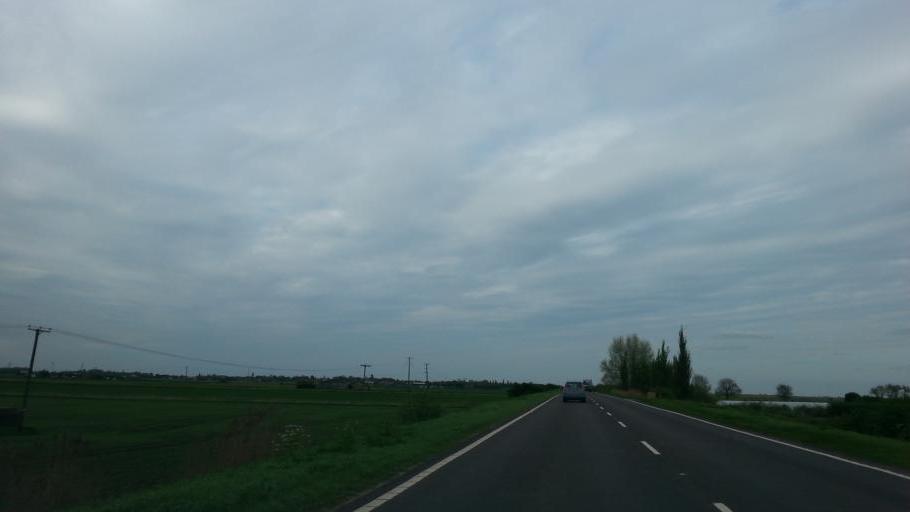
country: GB
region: England
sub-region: Cambridgeshire
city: Chatteris
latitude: 52.4717
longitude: 0.0495
